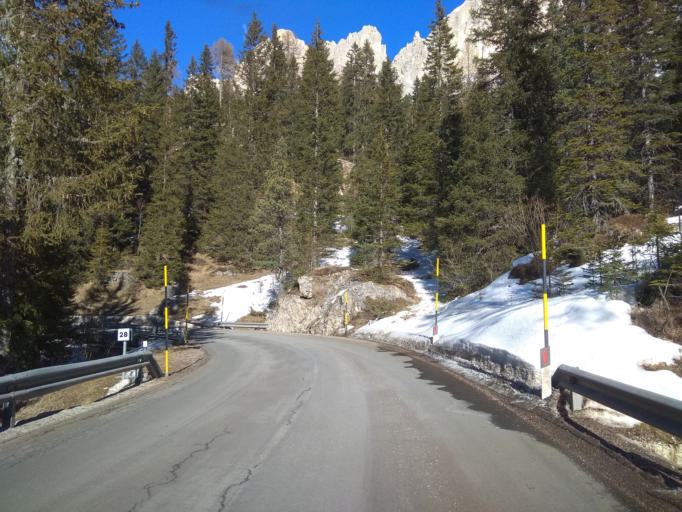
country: IT
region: Trentino-Alto Adige
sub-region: Bolzano
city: Nova Levante
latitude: 46.4196
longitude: 11.6012
